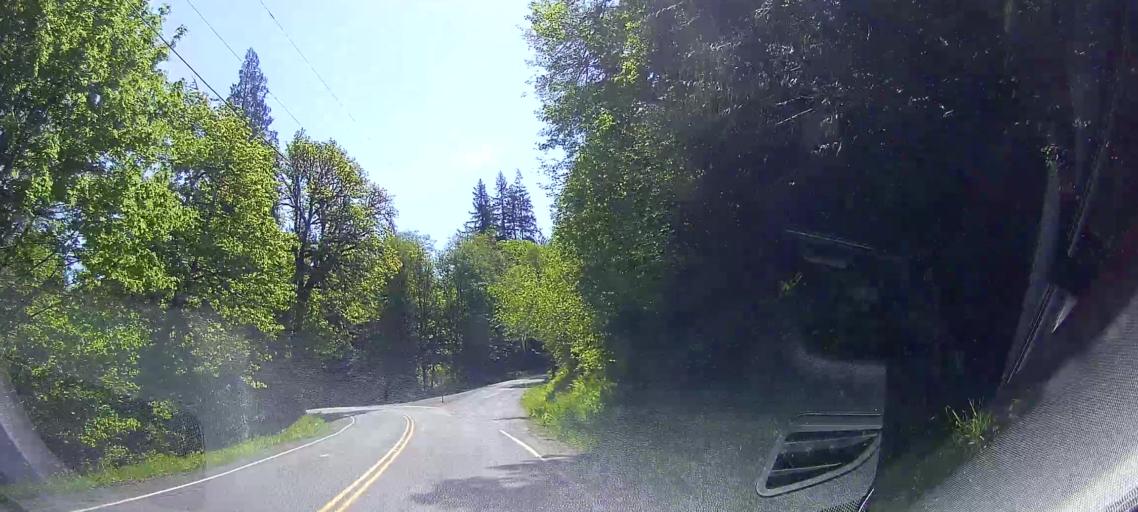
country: US
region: Washington
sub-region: Snohomish County
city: Darrington
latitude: 48.4731
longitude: -121.6425
